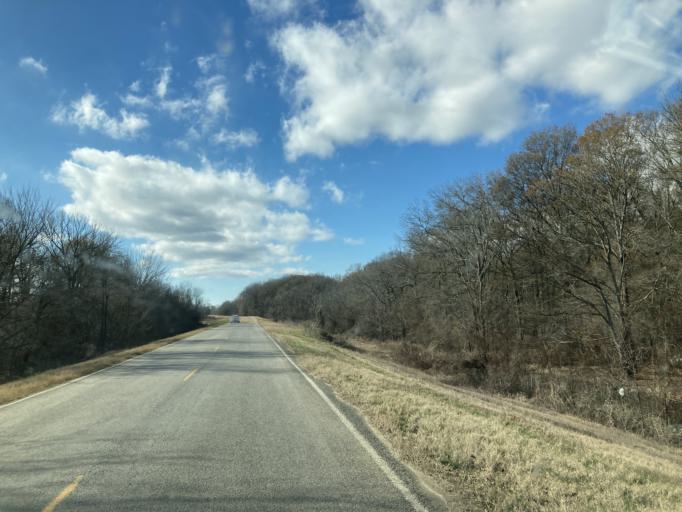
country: US
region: Mississippi
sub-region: Yazoo County
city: Yazoo City
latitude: 32.9653
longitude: -90.4608
